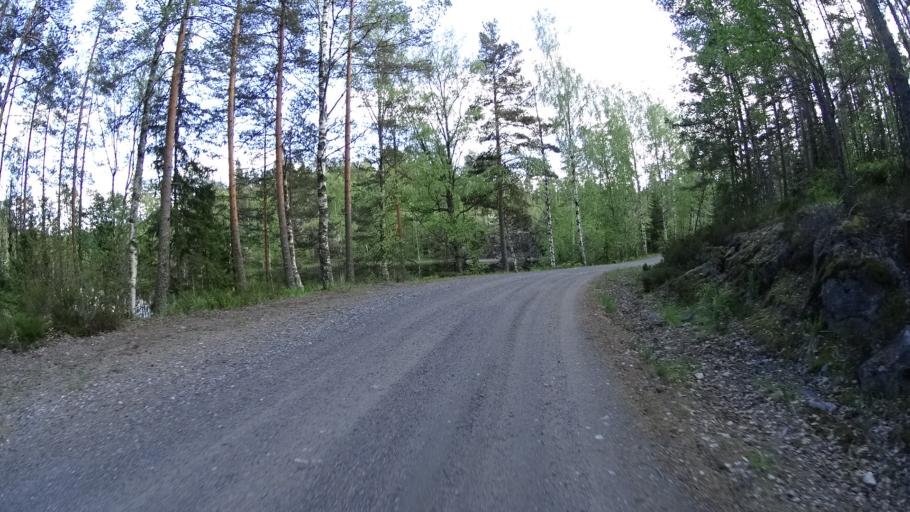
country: FI
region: Uusimaa
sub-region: Raaseporin
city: Pohja
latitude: 60.1589
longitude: 23.4914
